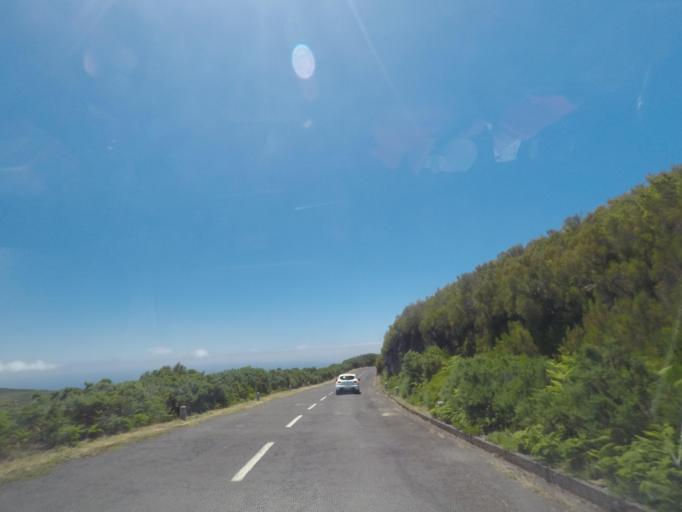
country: PT
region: Madeira
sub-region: Calheta
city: Faja da Ovelha
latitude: 32.8066
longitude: -17.1951
